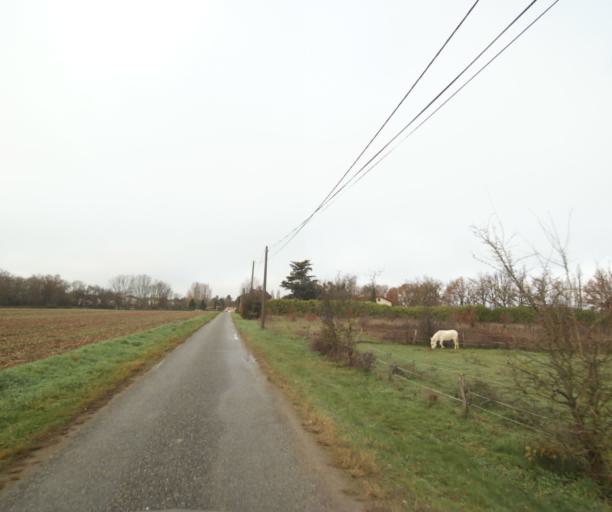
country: FR
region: Midi-Pyrenees
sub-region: Departement de la Haute-Garonne
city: Villemur-sur-Tarn
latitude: 43.8759
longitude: 1.4702
